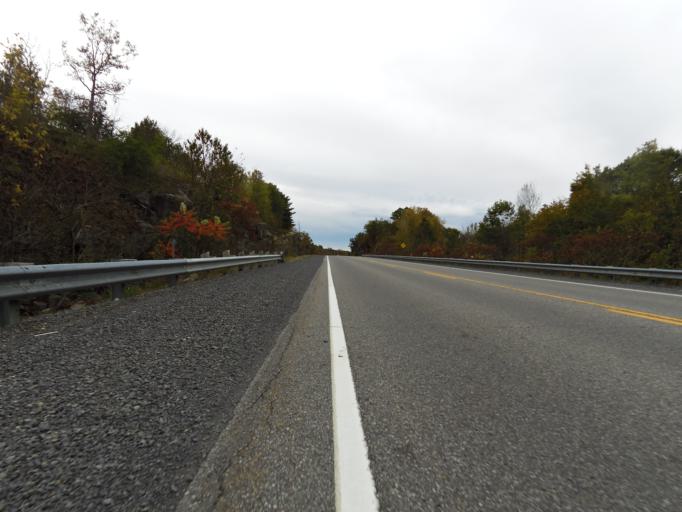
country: CA
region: Ontario
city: Gananoque
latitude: 44.4020
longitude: -76.3128
